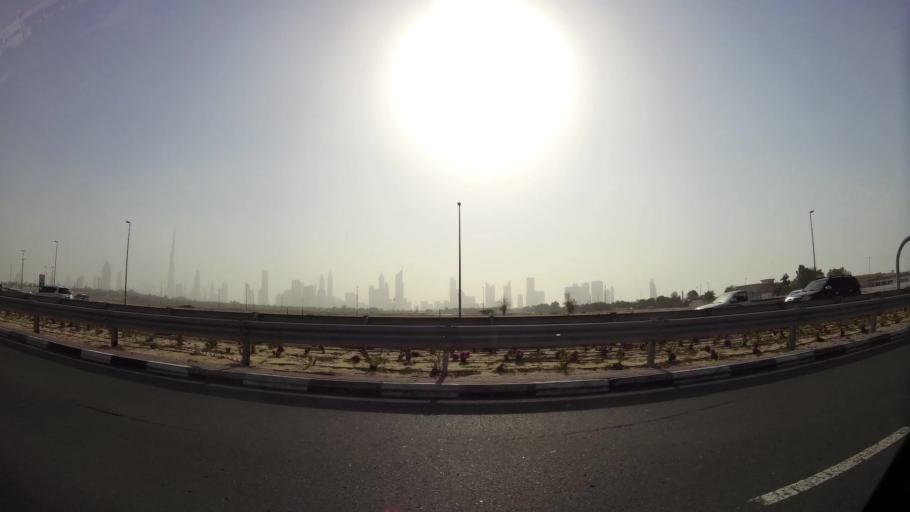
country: AE
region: Ash Shariqah
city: Sharjah
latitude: 25.2171
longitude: 55.3146
